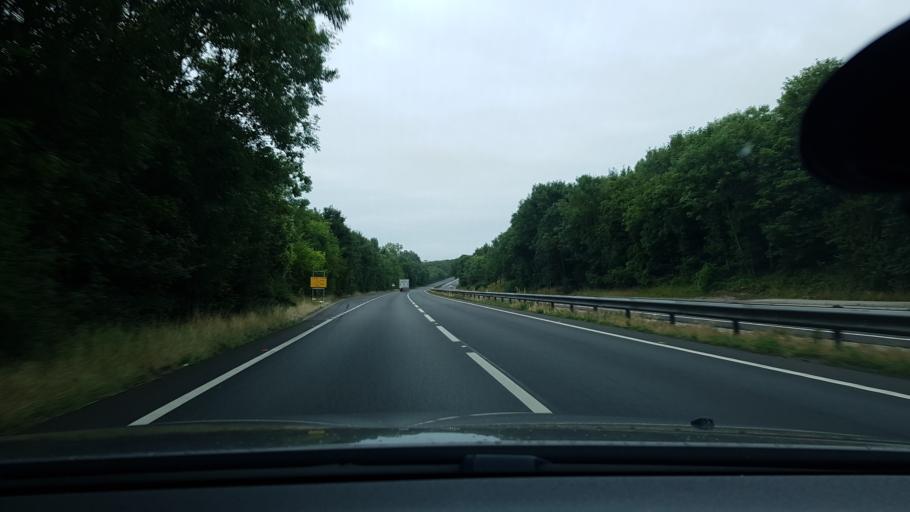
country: GB
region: England
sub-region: Hampshire
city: Overton
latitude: 51.2252
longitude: -1.3453
